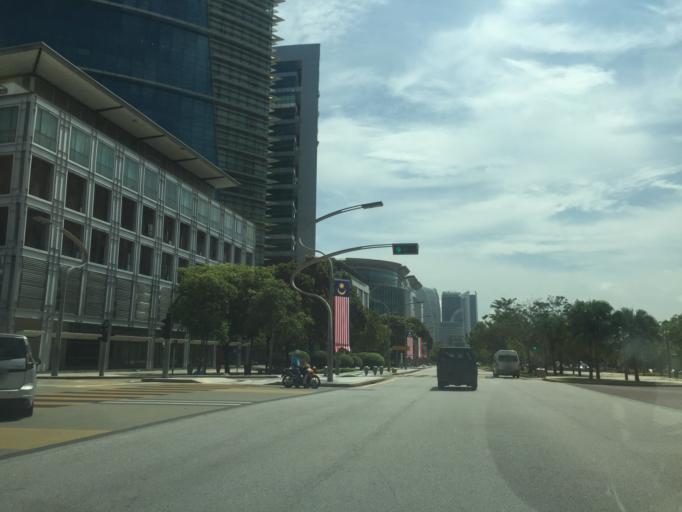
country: MY
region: Putrajaya
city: Putrajaya
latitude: 2.9156
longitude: 101.6845
